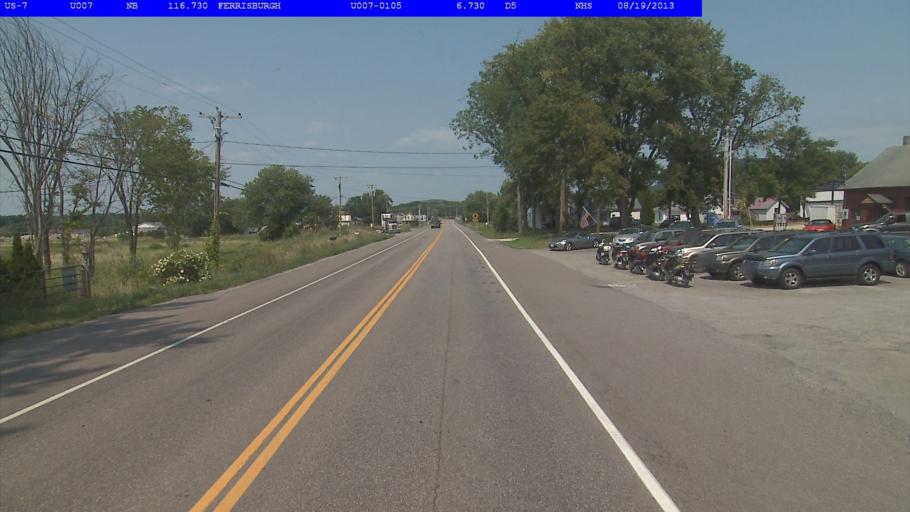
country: US
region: Vermont
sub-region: Addison County
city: Vergennes
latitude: 44.2548
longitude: -73.2277
